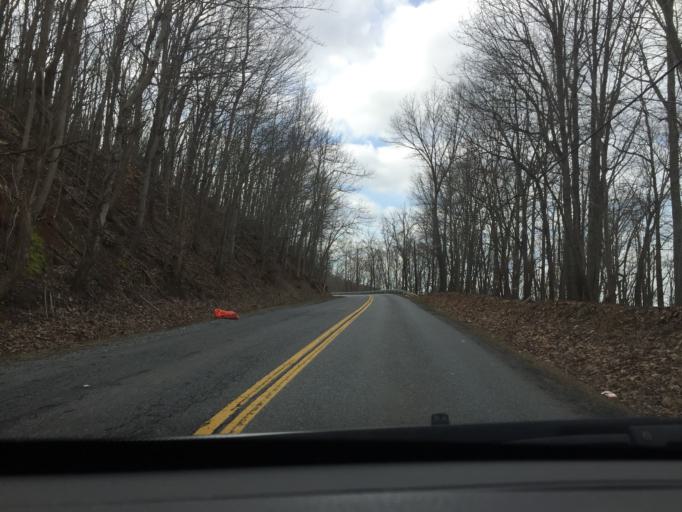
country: US
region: Virginia
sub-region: City of Lynchburg
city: West Lynchburg
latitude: 37.3512
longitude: -79.1698
